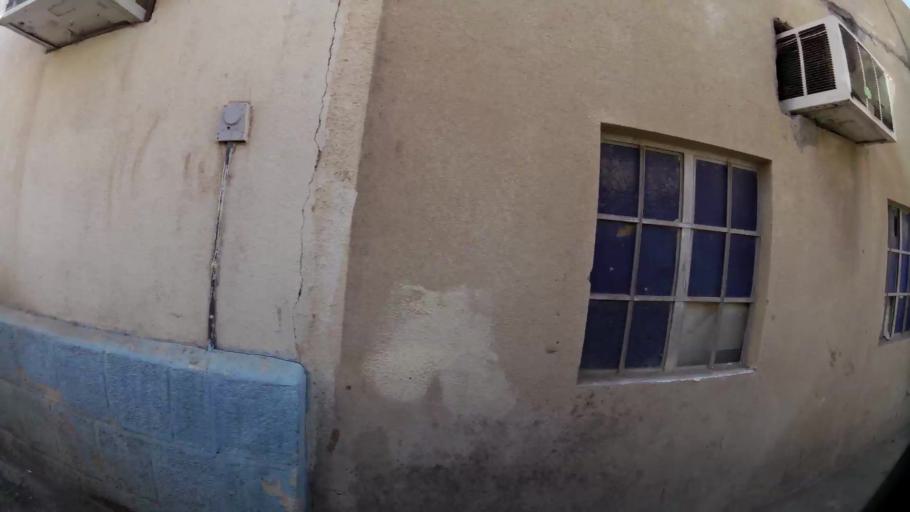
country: OM
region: Muhafazat Masqat
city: Muscat
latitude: 23.5848
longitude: 58.5173
